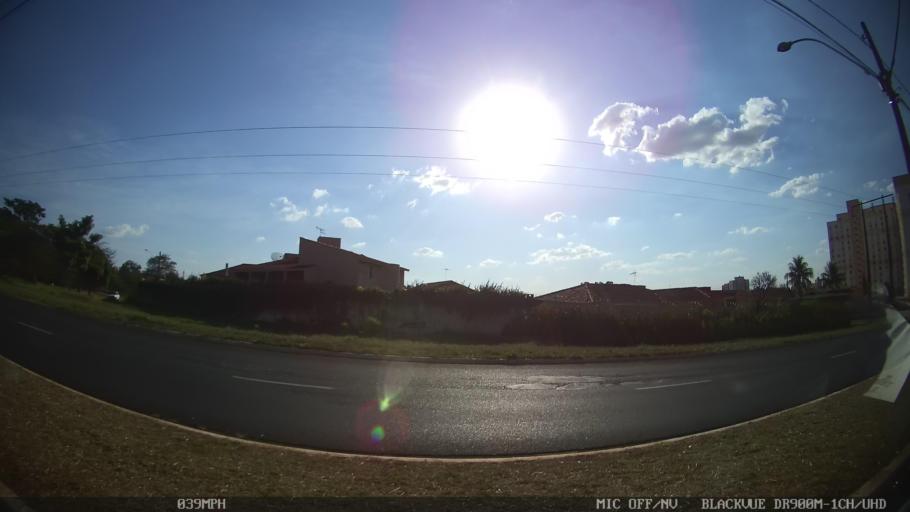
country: BR
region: Sao Paulo
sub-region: Ribeirao Preto
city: Ribeirao Preto
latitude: -21.2004
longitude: -47.7804
